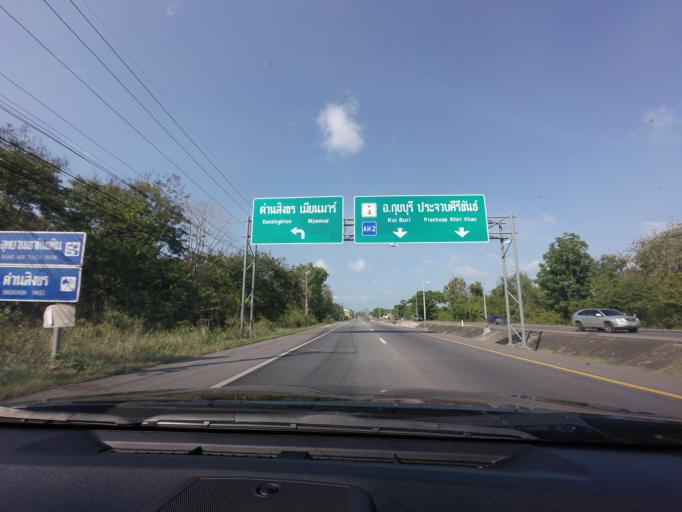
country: TH
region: Prachuap Khiri Khan
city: Prachuap Khiri Khan
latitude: 11.7462
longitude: 99.7561
